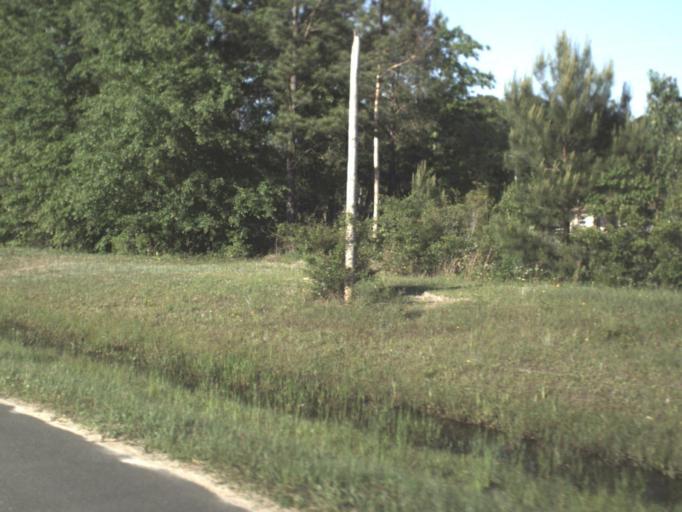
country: US
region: Florida
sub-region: Liberty County
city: Bristol
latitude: 30.3604
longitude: -84.8179
